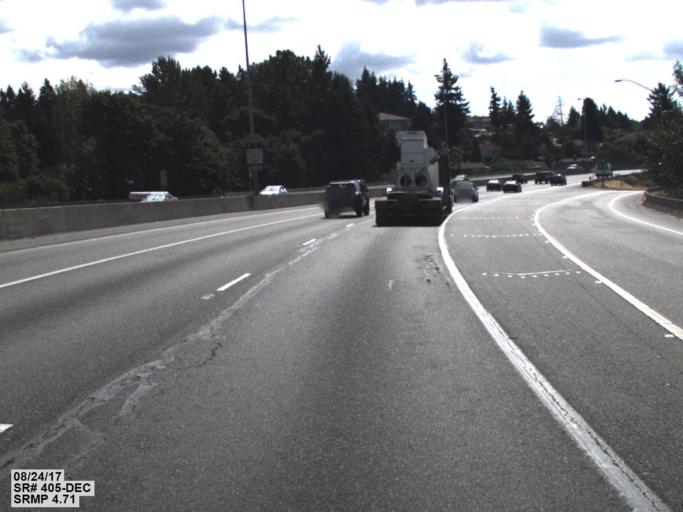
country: US
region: Washington
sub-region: King County
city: Renton
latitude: 47.4928
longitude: -122.1918
